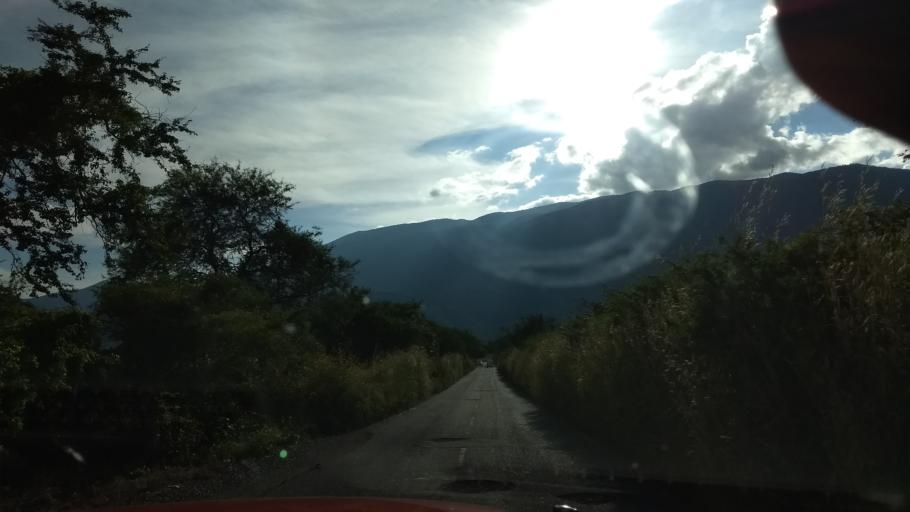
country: MX
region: Colima
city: Suchitlan
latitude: 19.4506
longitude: -103.8121
